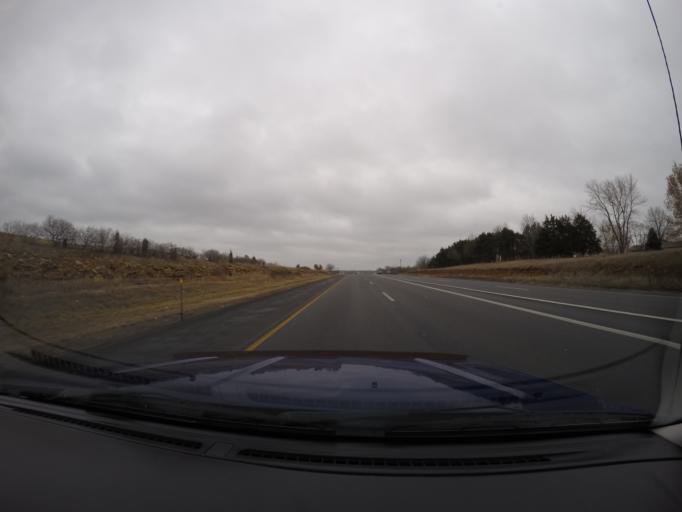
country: US
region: Kansas
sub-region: Shawnee County
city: Topeka
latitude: 39.0309
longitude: -95.5855
